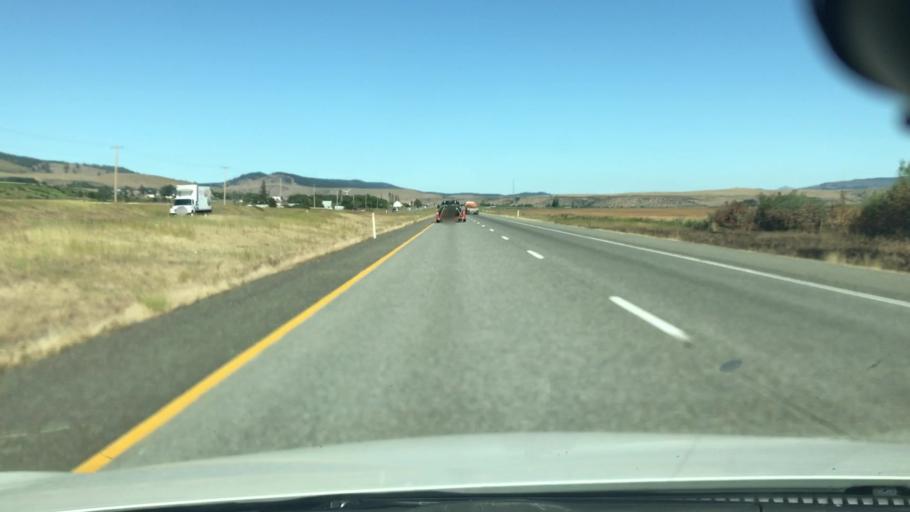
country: US
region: Washington
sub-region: Kittitas County
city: Ellensburg
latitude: 47.0673
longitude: -120.7005
